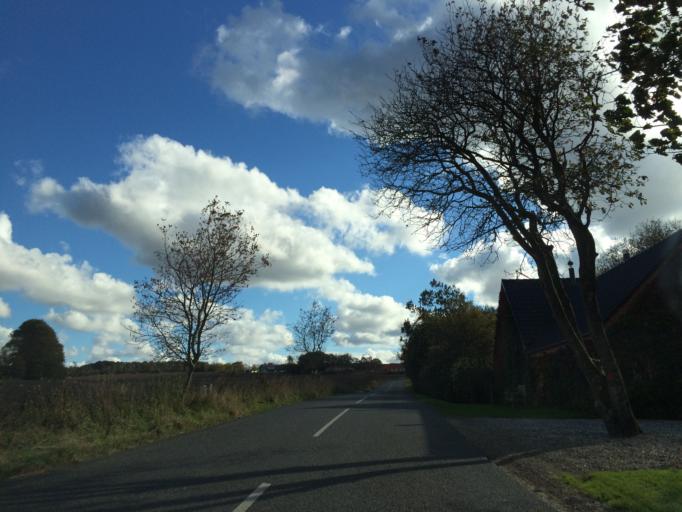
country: DK
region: Central Jutland
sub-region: Skanderborg Kommune
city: Ry
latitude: 56.1846
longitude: 9.7707
